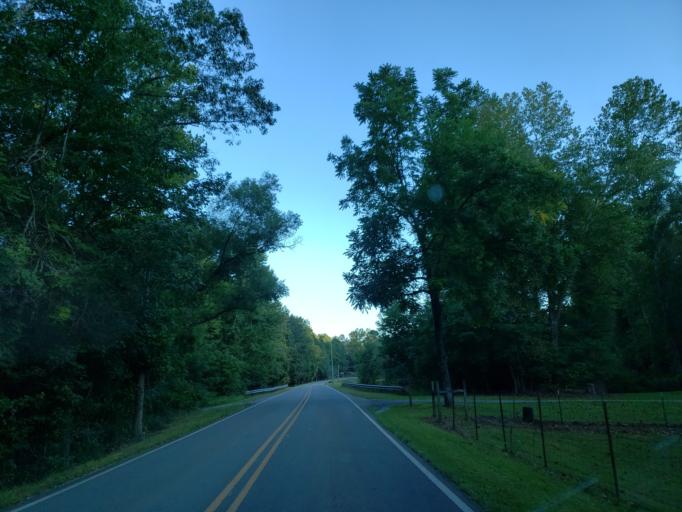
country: US
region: Georgia
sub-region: Bartow County
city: Rydal
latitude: 34.3866
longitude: -84.5916
